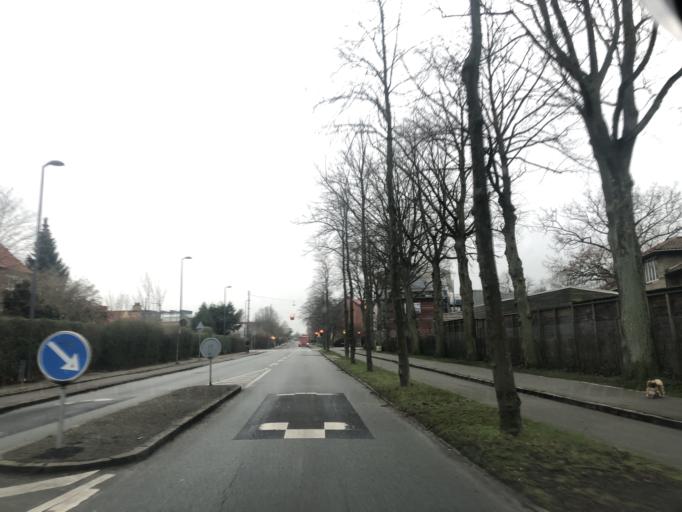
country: DK
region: Capital Region
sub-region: Tarnby Kommune
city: Tarnby
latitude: 55.6471
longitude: 12.6051
